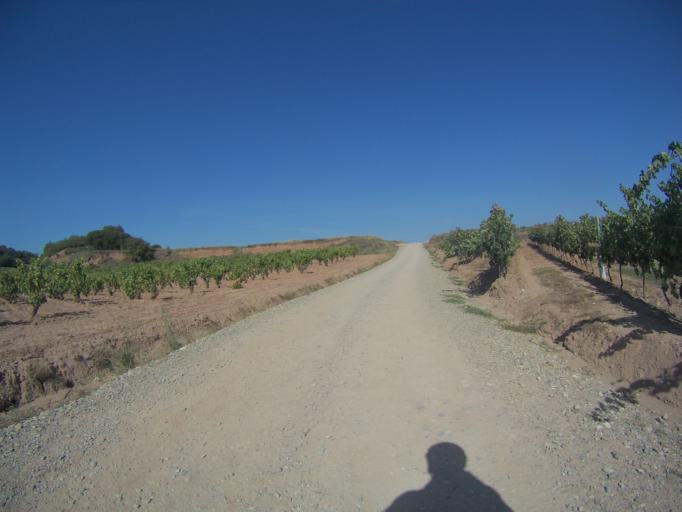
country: ES
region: La Rioja
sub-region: Provincia de La Rioja
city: Ventosa
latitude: 42.4103
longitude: -2.6332
